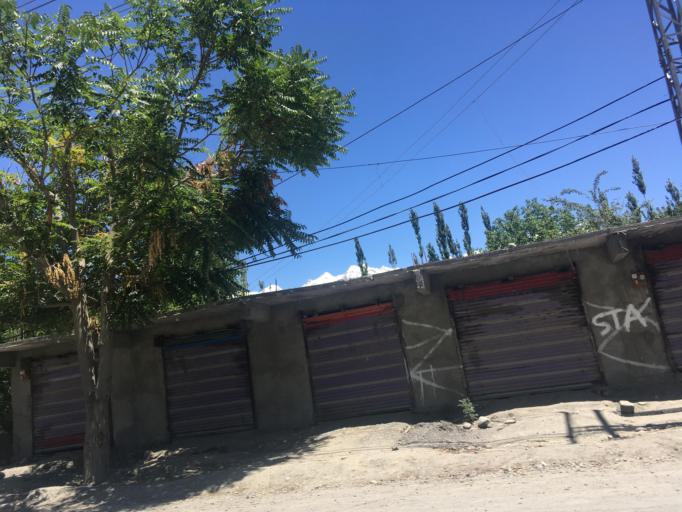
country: PK
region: Gilgit-Baltistan
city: Skardu
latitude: 35.3018
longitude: 75.5521
